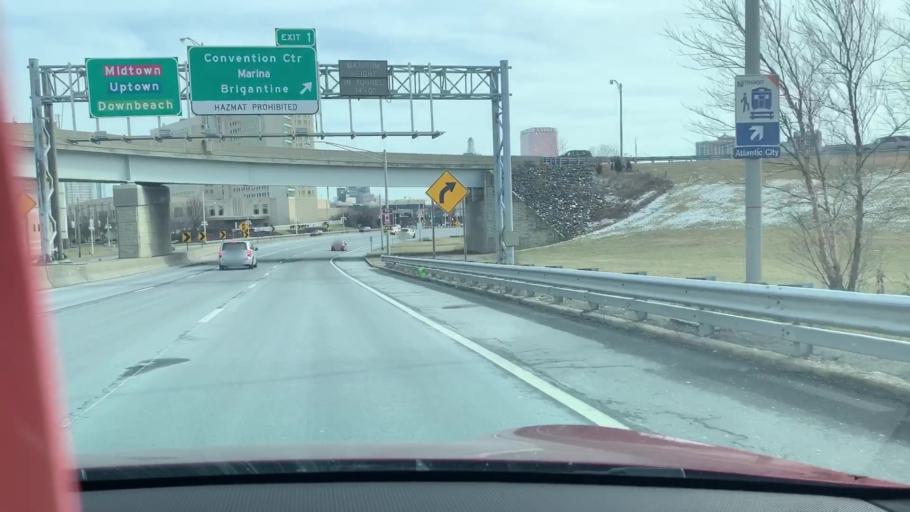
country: US
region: New Jersey
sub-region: Atlantic County
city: Atlantic City
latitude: 39.3628
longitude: -74.4420
